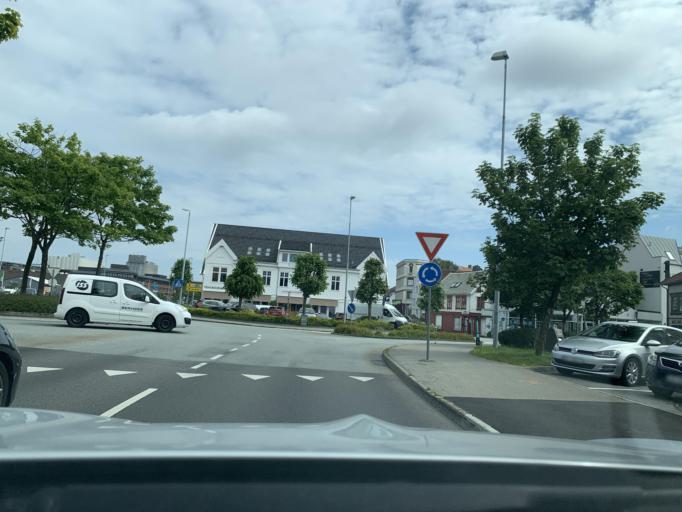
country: NO
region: Rogaland
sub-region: Stavanger
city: Stavanger
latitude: 58.9715
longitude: 5.7392
